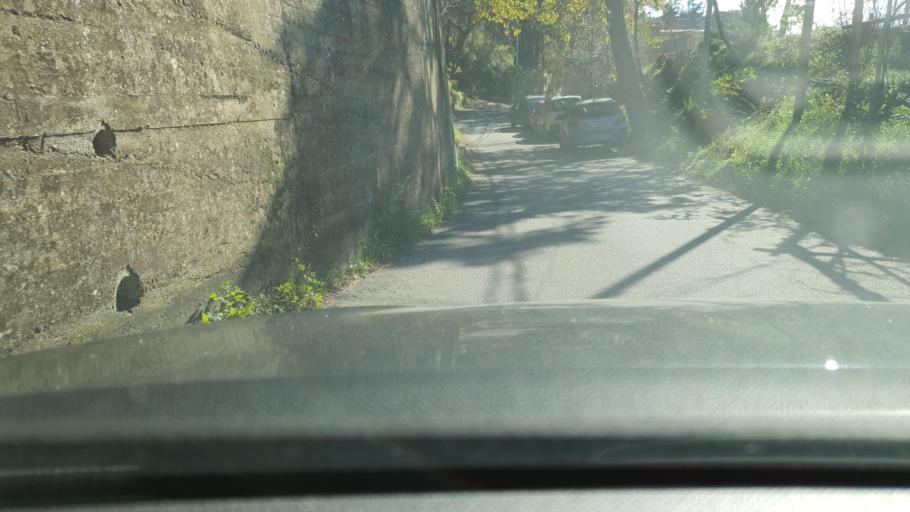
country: IT
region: Calabria
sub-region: Provincia di Catanzaro
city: Sant'Elia
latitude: 38.9561
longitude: 16.5812
